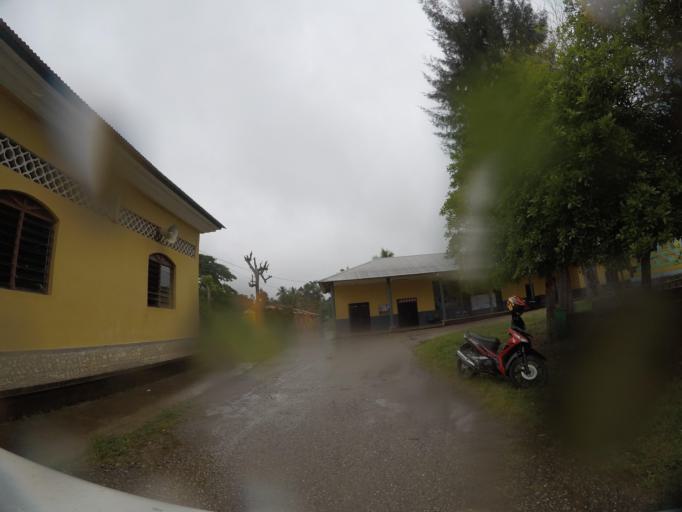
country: TL
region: Lautem
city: Lospalos
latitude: -8.5220
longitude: 126.9964
